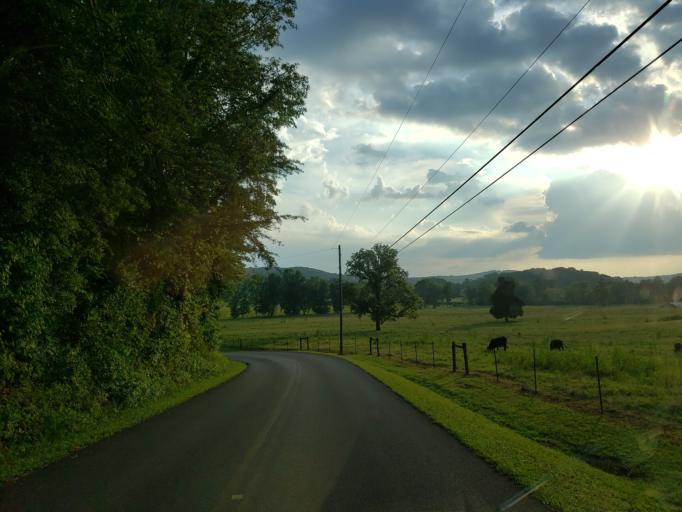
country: US
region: Georgia
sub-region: Polk County
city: Aragon
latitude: 34.0591
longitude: -84.9804
